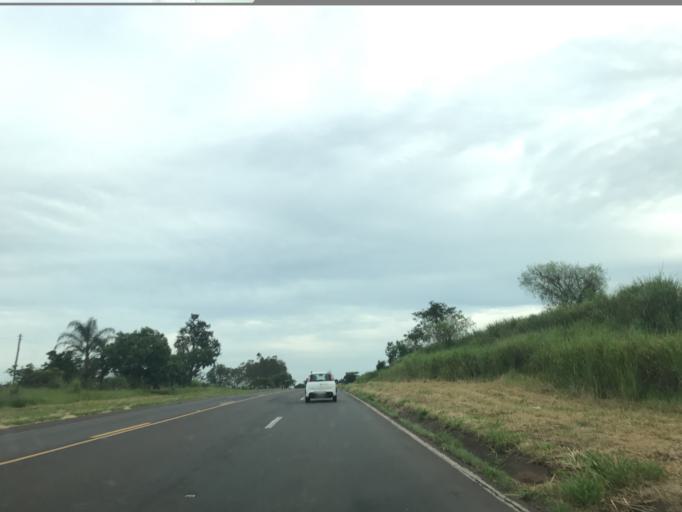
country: BR
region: Sao Paulo
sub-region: Tupa
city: Tupa
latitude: -21.6070
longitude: -50.4726
